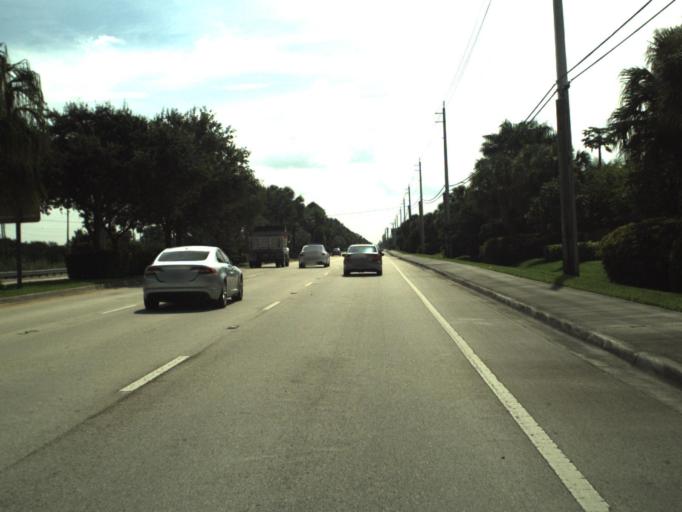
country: US
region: Florida
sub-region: Broward County
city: Sunshine Ranches
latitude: 26.0635
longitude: -80.3038
